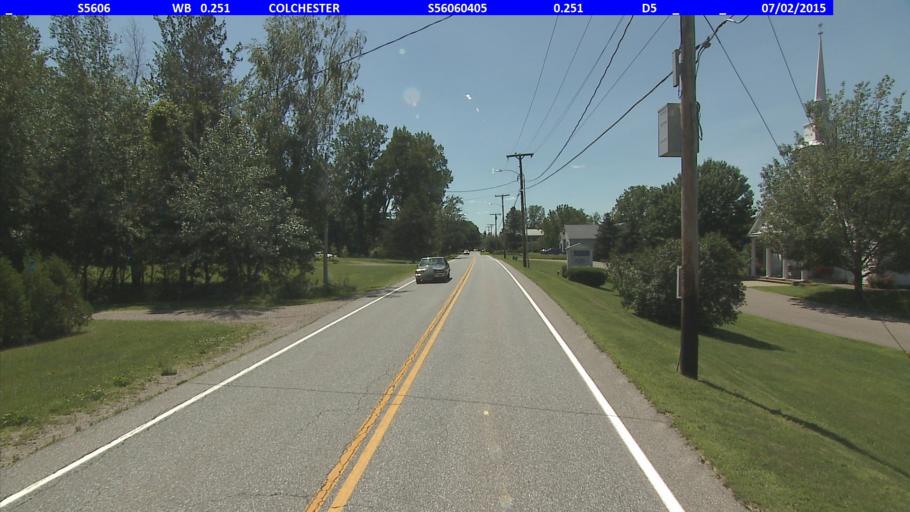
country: US
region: Vermont
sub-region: Chittenden County
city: Burlington
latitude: 44.5522
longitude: -73.2449
